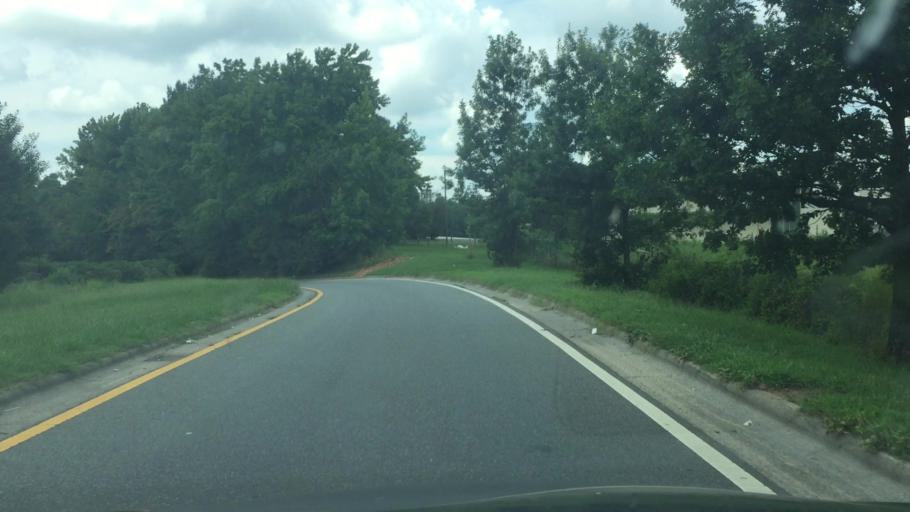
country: US
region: North Carolina
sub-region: Randolph County
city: Asheboro
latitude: 35.6868
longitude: -79.8286
